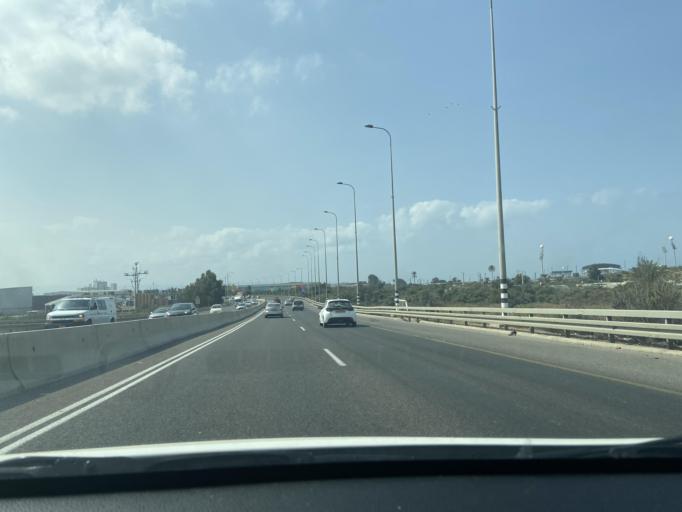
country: IL
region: Northern District
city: `Akko
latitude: 32.9092
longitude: 35.0934
